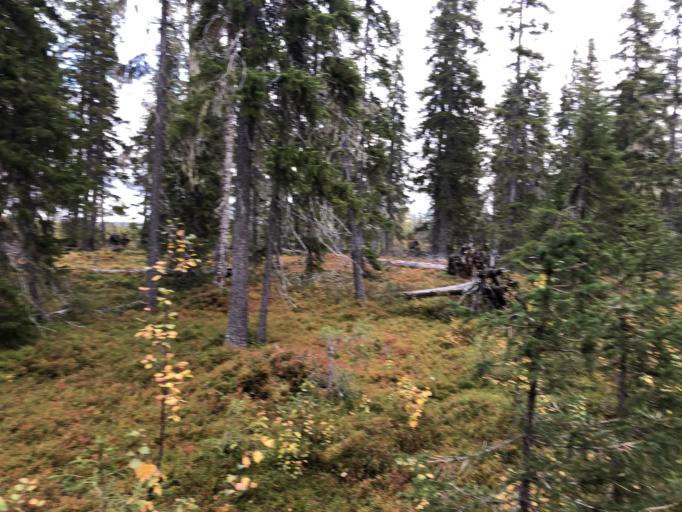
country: FI
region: Northern Ostrobothnia
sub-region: Koillismaa
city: Kuusamo
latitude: 65.8954
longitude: 28.8109
